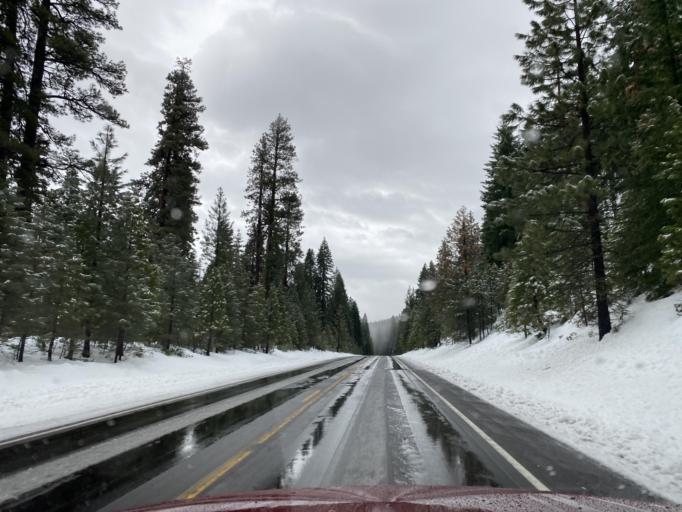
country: US
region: Oregon
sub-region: Klamath County
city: Klamath Falls
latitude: 42.5313
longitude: -122.0899
